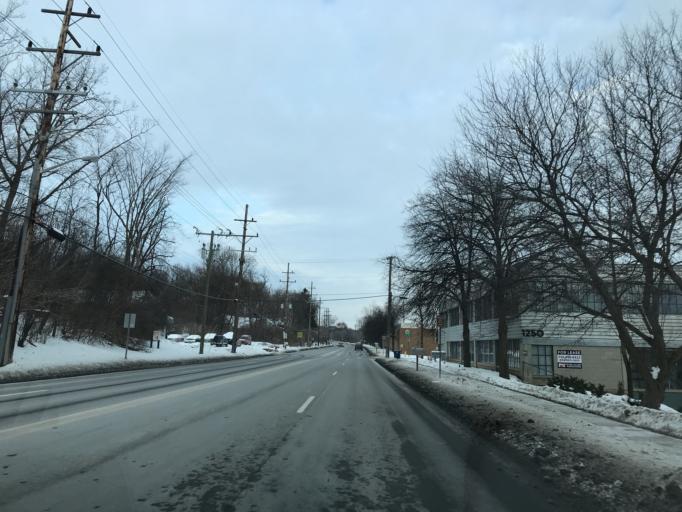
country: US
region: Michigan
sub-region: Washtenaw County
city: Ann Arbor
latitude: 42.2944
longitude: -83.7469
